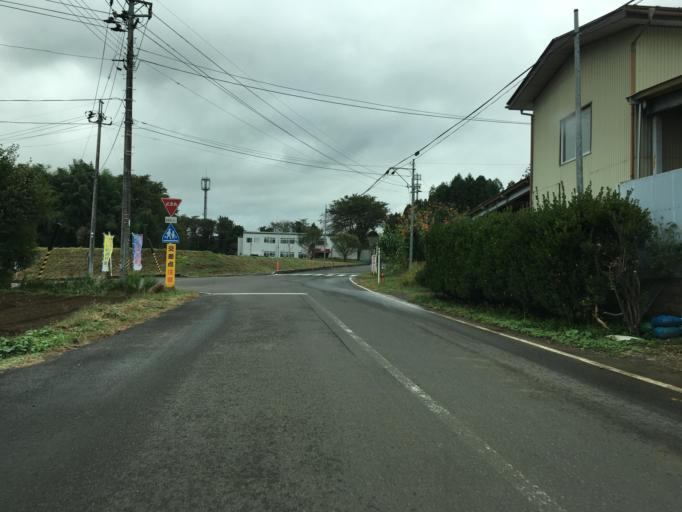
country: JP
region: Fukushima
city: Nihommatsu
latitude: 37.6202
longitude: 140.4387
